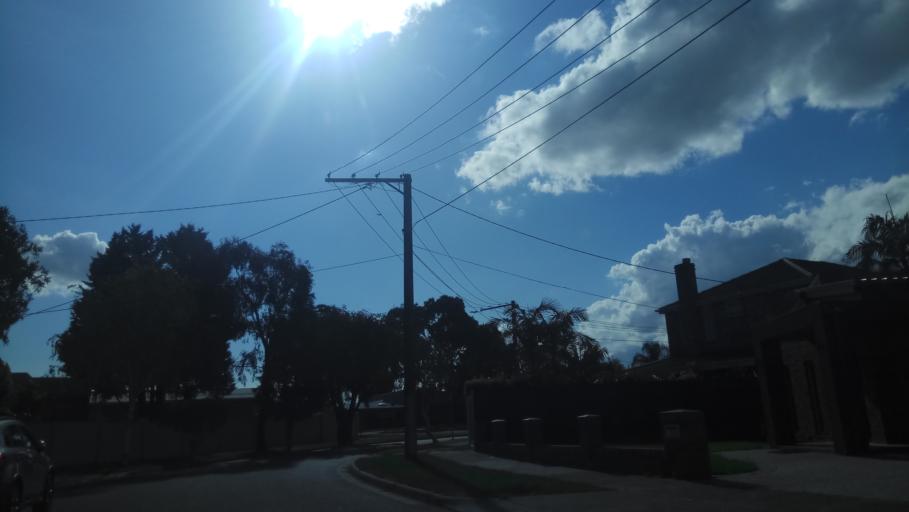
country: AU
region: Victoria
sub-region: Kingston
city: Dingley Village
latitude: -37.9868
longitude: 145.1305
